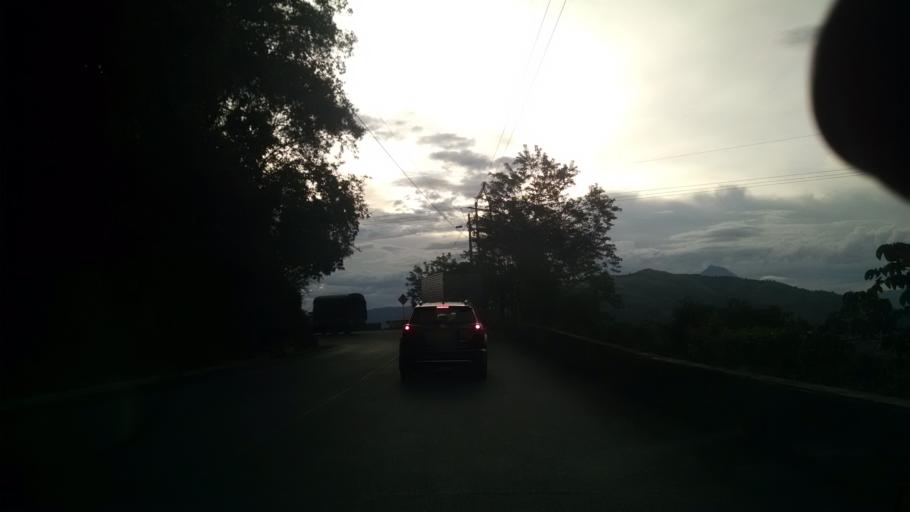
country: CO
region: Antioquia
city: Santa Barbara
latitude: 5.8497
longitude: -75.5758
